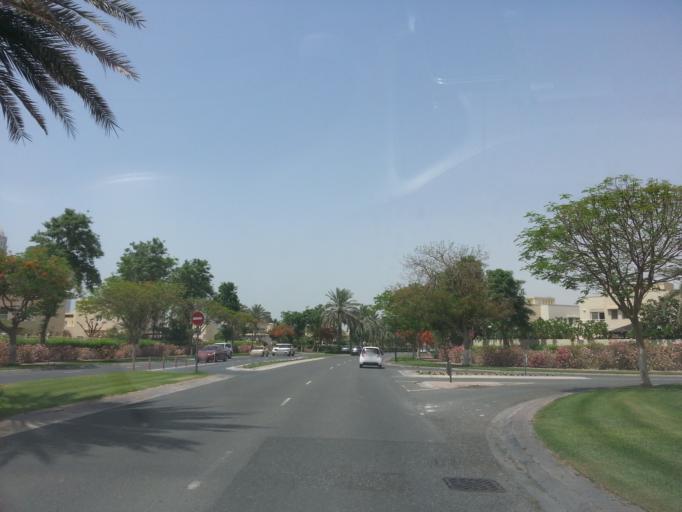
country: AE
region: Dubai
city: Dubai
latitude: 25.0691
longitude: 55.1551
